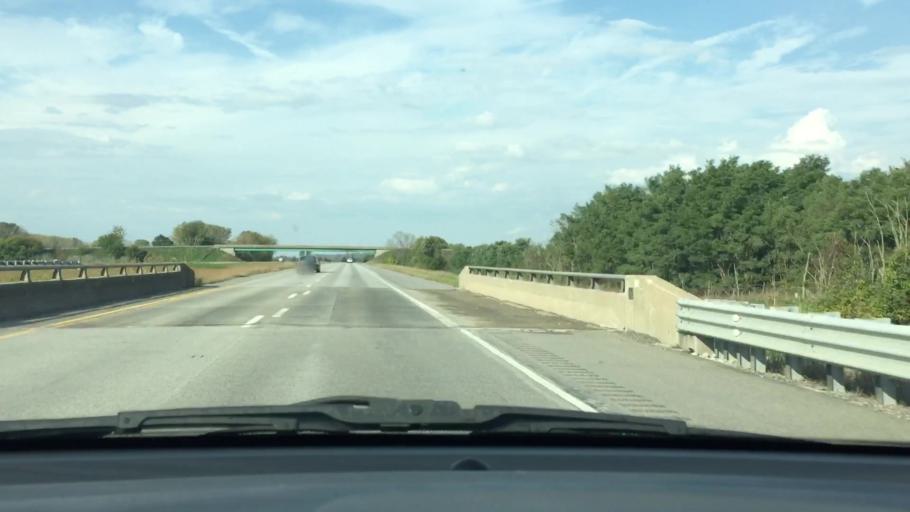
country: US
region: Illinois
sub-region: Rock Island County
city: Port Byron
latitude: 41.5415
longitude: -90.2715
